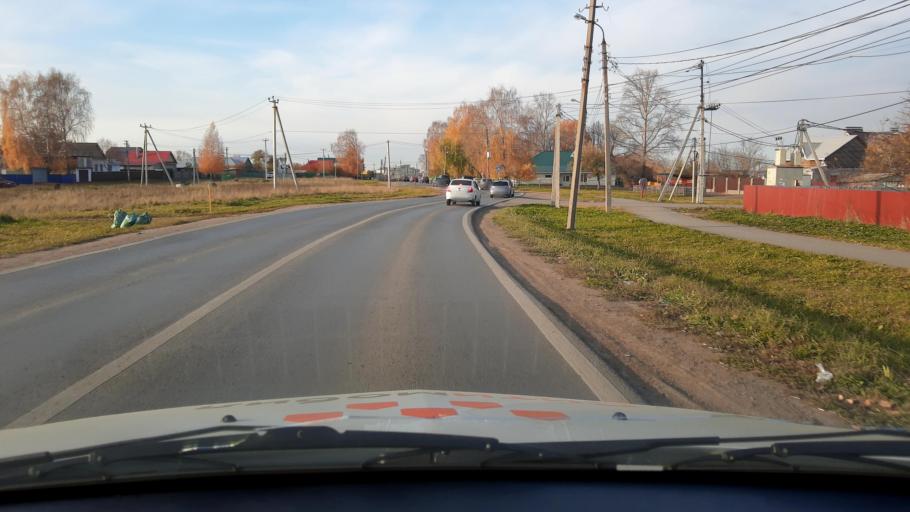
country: RU
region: Bashkortostan
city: Iglino
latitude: 54.7874
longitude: 56.2324
